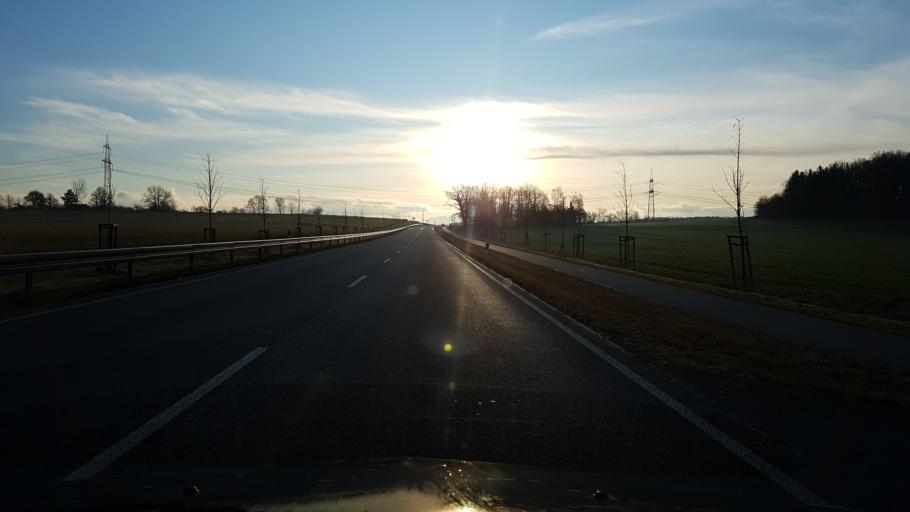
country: DE
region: Saxony
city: Radibor
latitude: 51.2449
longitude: 14.3597
